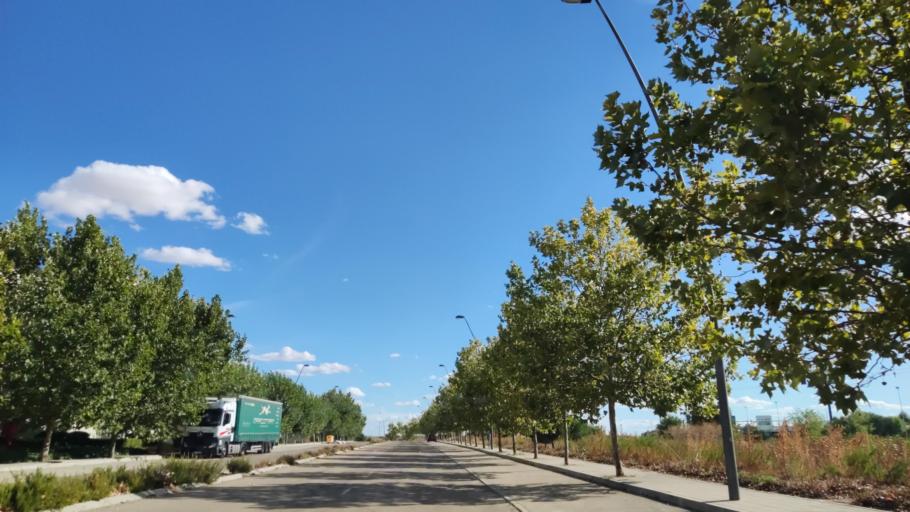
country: ES
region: Madrid
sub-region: Provincia de Madrid
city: Pinto
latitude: 40.2840
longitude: -3.6901
